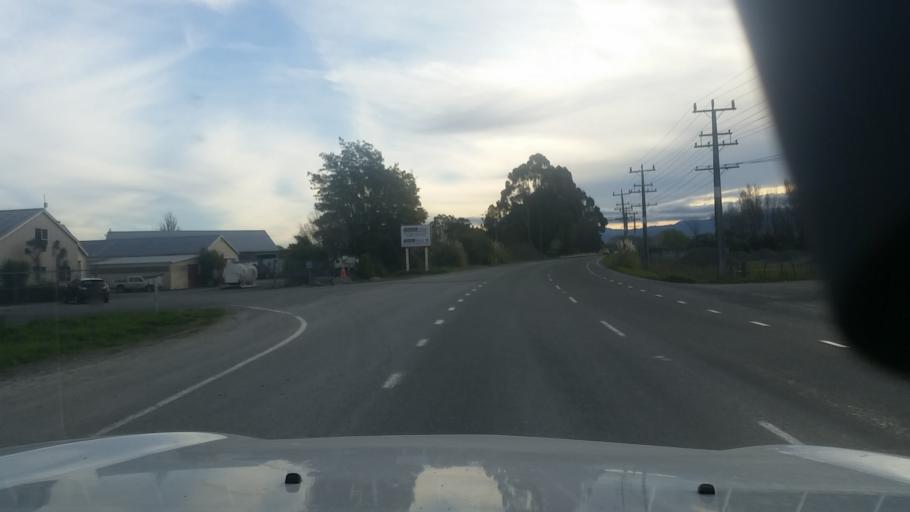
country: NZ
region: Wellington
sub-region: Masterton District
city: Masterton
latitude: -40.9501
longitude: 175.6917
